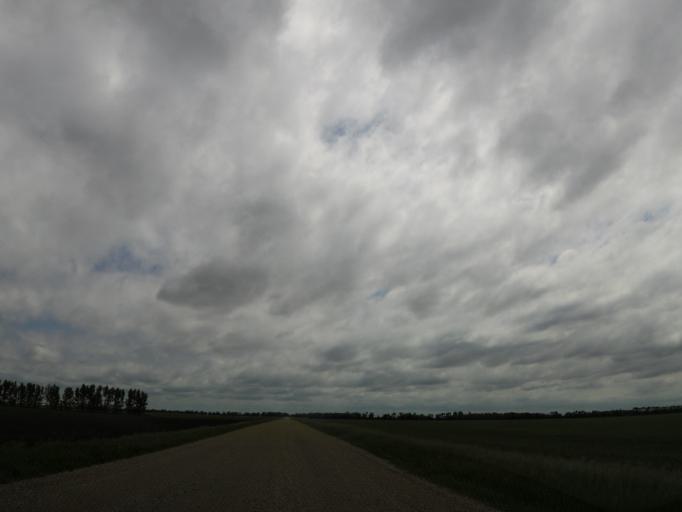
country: US
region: North Dakota
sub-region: Walsh County
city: Grafton
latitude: 48.4374
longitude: -97.4917
